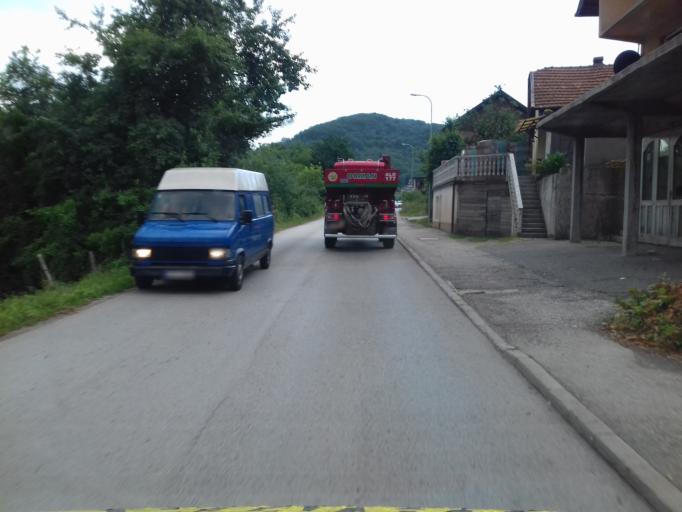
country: BA
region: Federation of Bosnia and Herzegovina
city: Visoko
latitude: 43.9672
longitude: 18.1838
